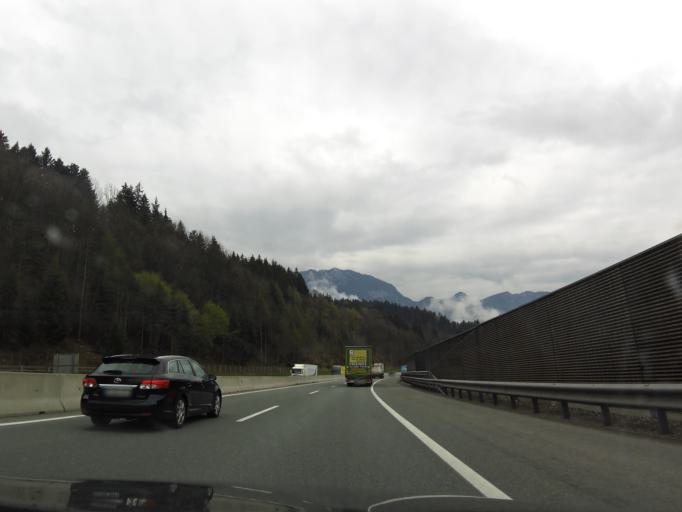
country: AT
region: Tyrol
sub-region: Politischer Bezirk Kufstein
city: Angath
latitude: 47.5017
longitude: 12.0581
